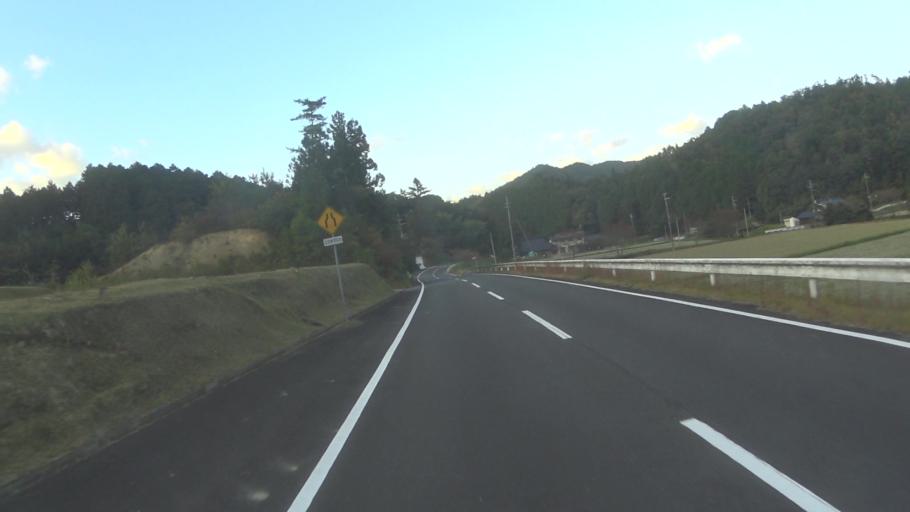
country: JP
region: Kyoto
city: Ayabe
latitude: 35.2805
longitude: 135.2376
